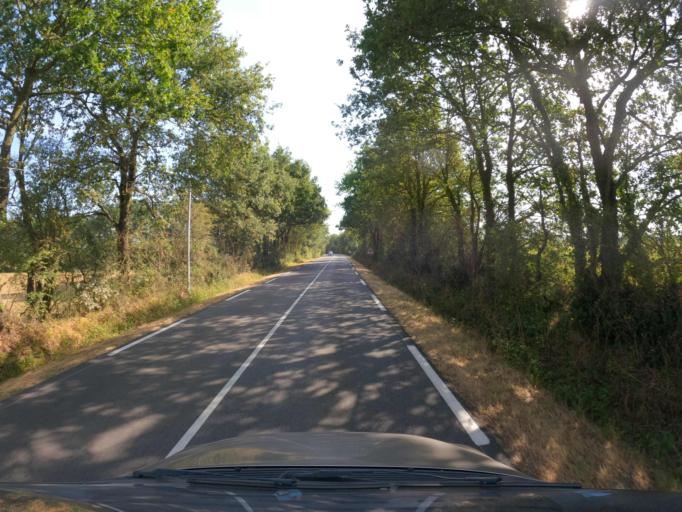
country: FR
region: Pays de la Loire
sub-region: Departement de la Vendee
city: Saint-Christophe-du-Ligneron
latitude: 46.8034
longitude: -1.7828
